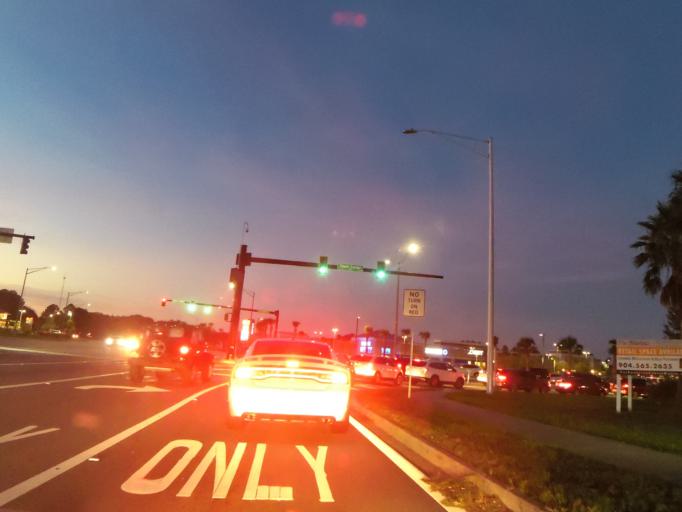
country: US
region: Florida
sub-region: Duval County
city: Jacksonville
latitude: 30.2542
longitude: -81.5361
